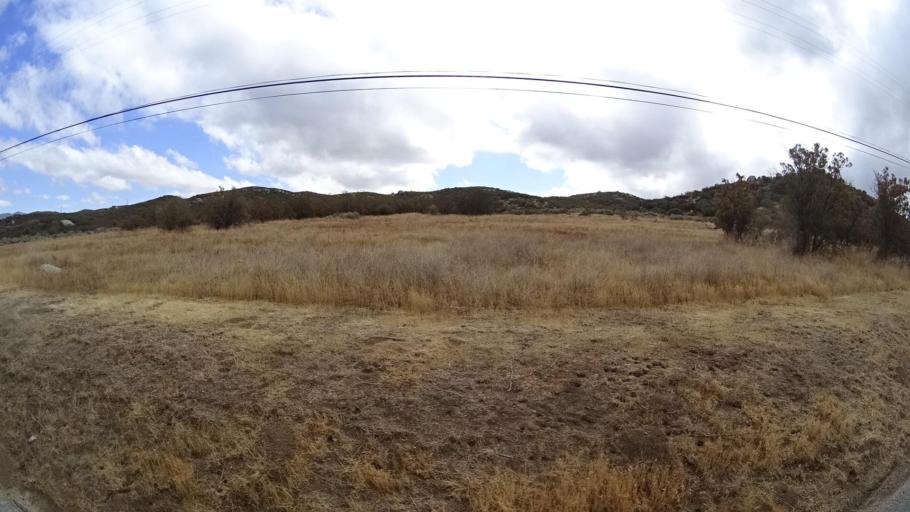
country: US
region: California
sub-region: San Diego County
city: Campo
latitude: 32.7109
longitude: -116.4308
